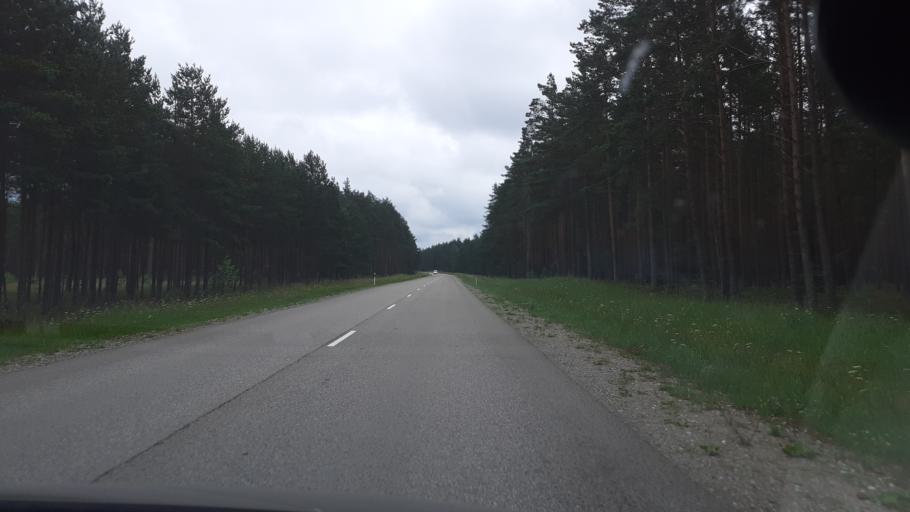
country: LV
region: Ventspils Rajons
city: Piltene
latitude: 57.1223
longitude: 21.7423
